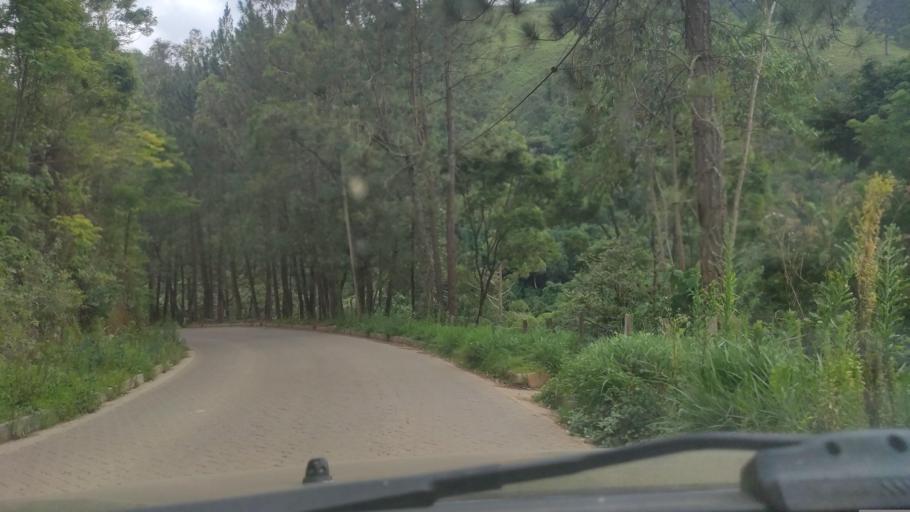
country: BR
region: Minas Gerais
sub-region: Paraisopolis
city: Paraisopolis
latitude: -22.6722
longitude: -45.8537
